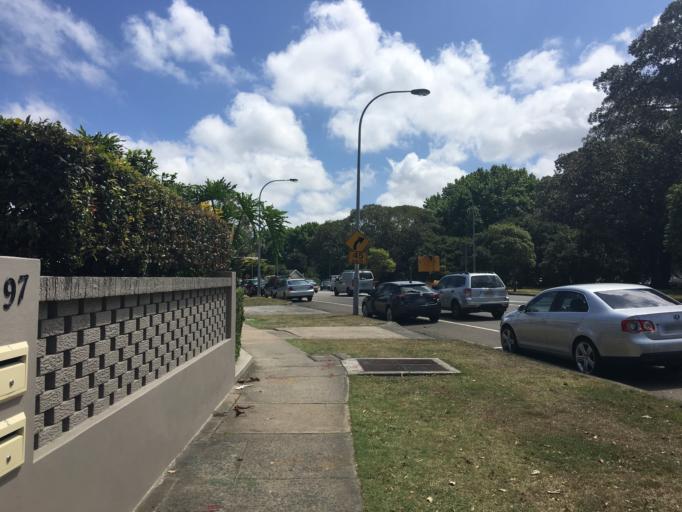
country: AU
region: New South Wales
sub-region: Waverley
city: Dover Heights
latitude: -33.8723
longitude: 151.2644
